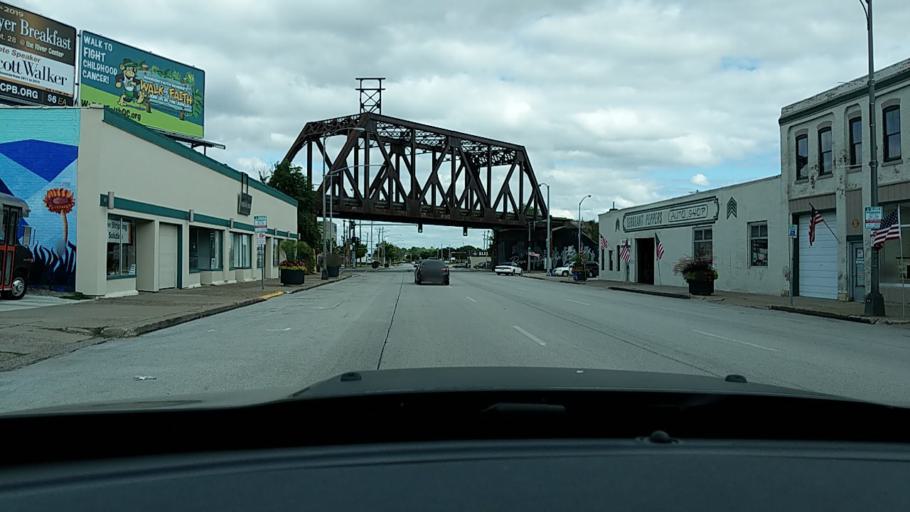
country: US
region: Iowa
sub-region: Scott County
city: Davenport
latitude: 41.5224
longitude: -90.5708
